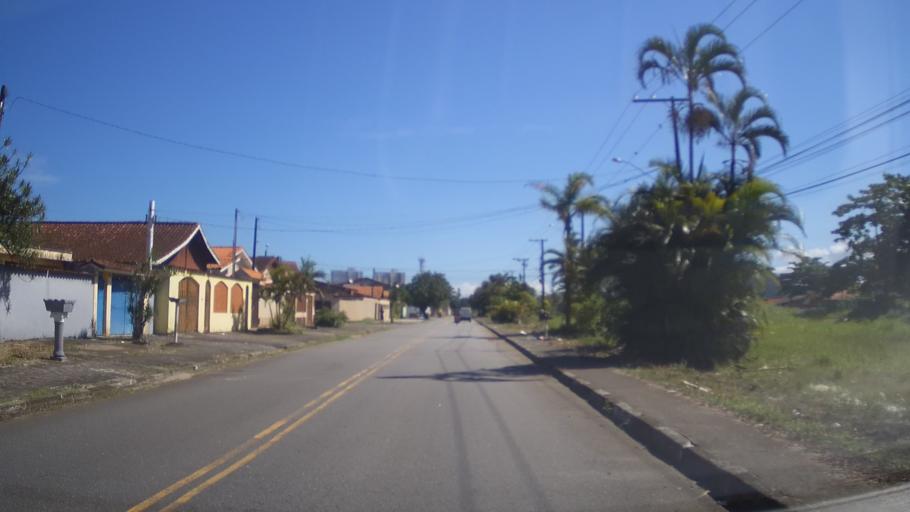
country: BR
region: Sao Paulo
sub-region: Mongagua
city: Mongagua
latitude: -24.1113
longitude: -46.6544
